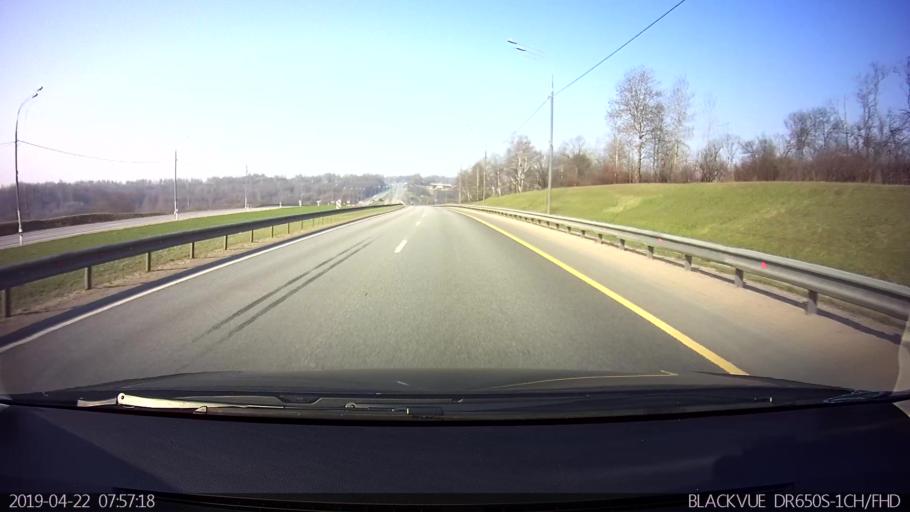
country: RU
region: Smolensk
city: Safonovo
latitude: 55.1366
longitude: 33.2135
